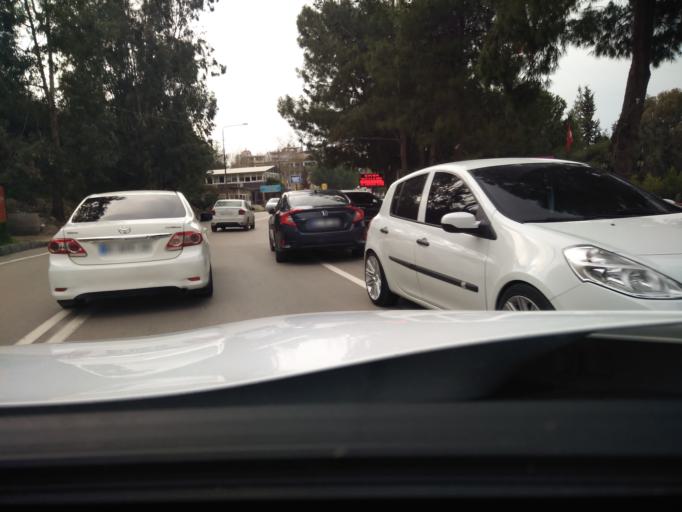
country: TR
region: Adana
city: Adana
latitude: 37.0585
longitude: 35.3021
